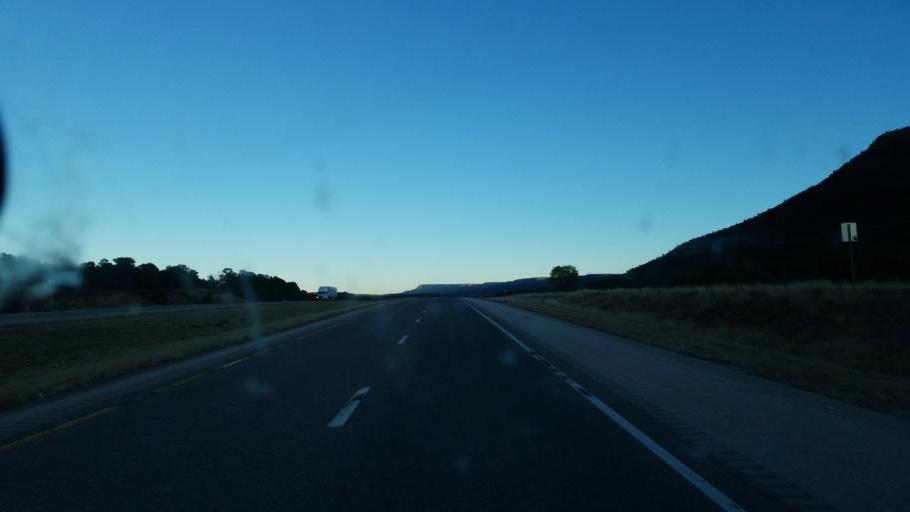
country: US
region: New Mexico
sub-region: San Miguel County
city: Pecos
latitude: 35.4751
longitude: -105.6591
